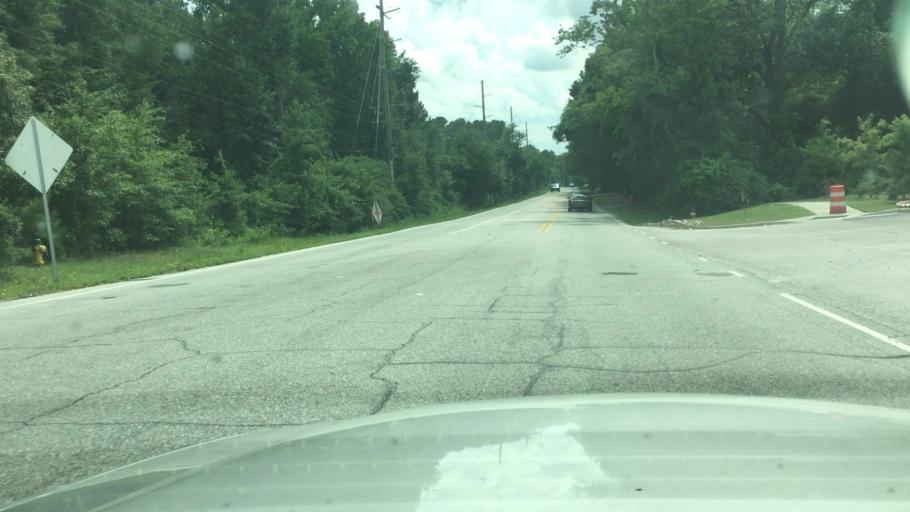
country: US
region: North Carolina
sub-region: Hoke County
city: Rockfish
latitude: 35.0148
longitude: -79.0092
